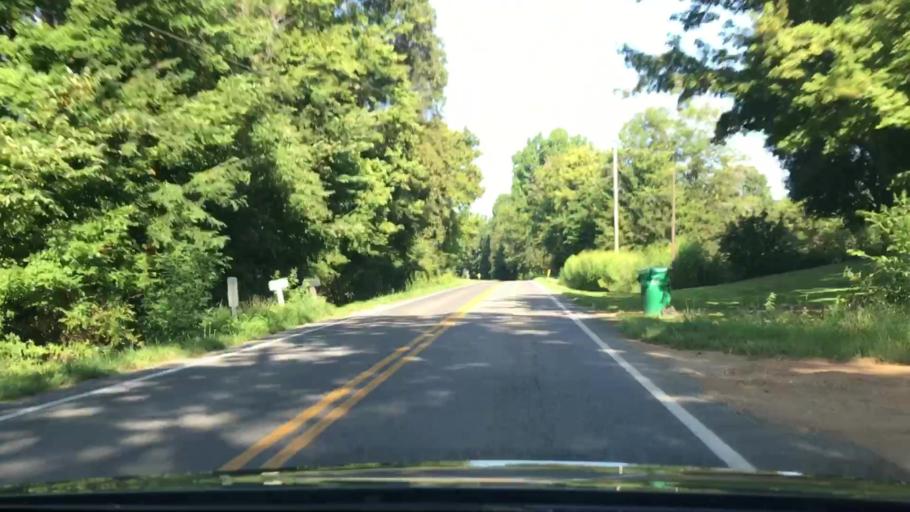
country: US
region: Kentucky
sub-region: Graves County
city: Mayfield
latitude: 36.7799
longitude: -88.5209
